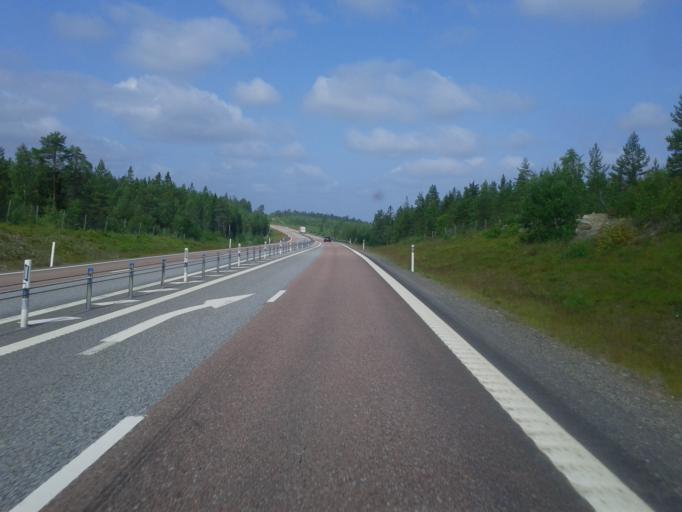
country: SE
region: Vaesterbotten
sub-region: Skelleftea Kommun
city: Soedra Bergsbyn
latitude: 64.6825
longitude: 21.0679
